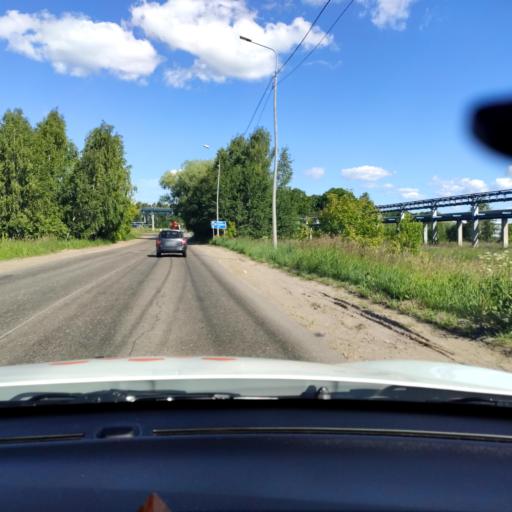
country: RU
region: Tatarstan
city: Staroye Arakchino
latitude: 55.8873
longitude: 48.9658
